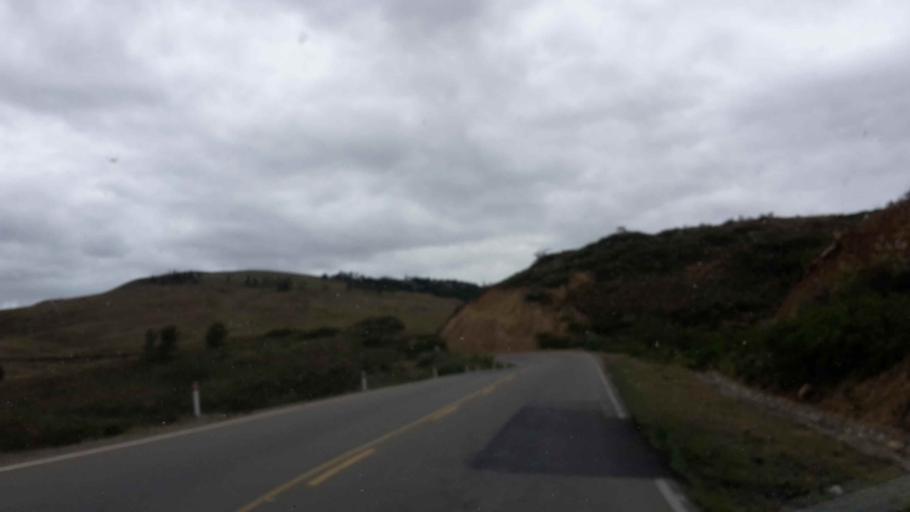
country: BO
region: Cochabamba
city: Punata
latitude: -17.4902
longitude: -65.7889
